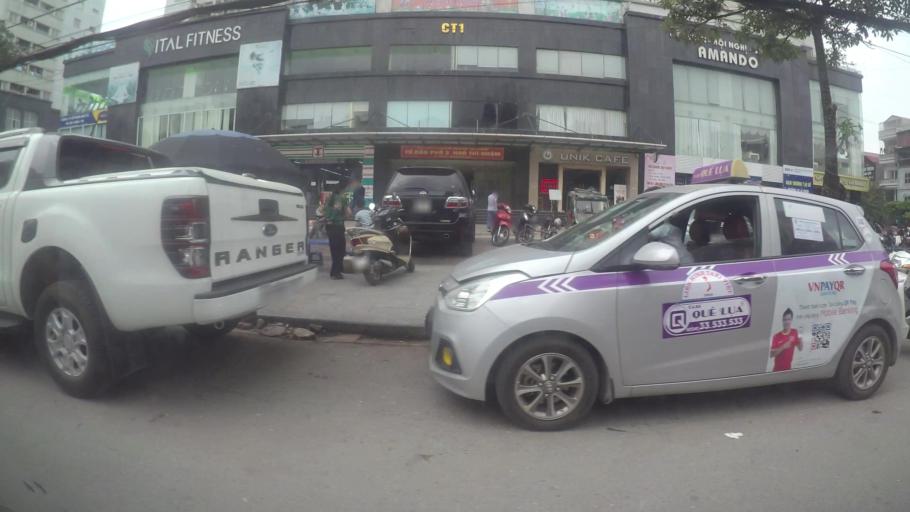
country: VN
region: Ha Noi
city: Ha Dong
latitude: 20.9695
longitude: 105.7685
